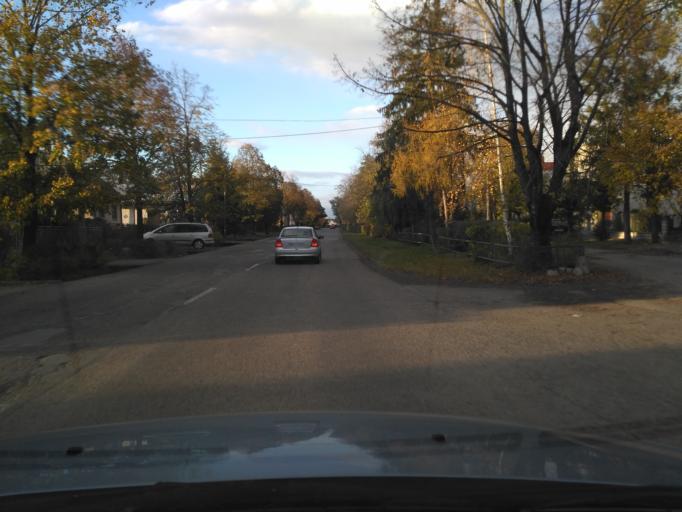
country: SK
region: Kosicky
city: Trebisov
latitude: 48.6466
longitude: 21.6797
